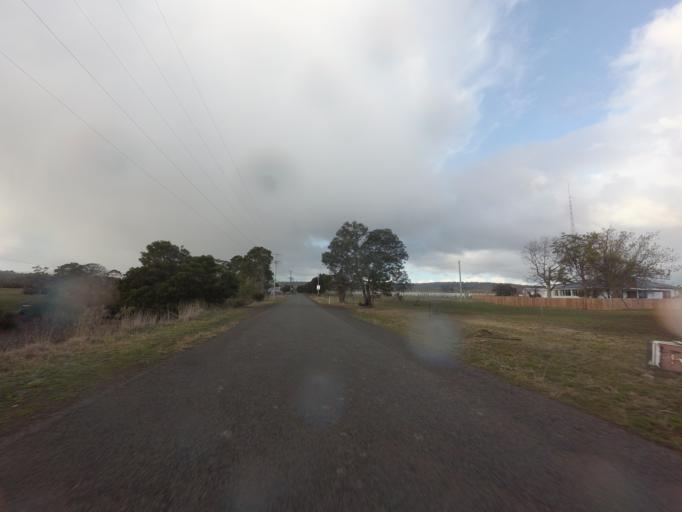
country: AU
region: Tasmania
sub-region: Break O'Day
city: St Helens
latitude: -42.0054
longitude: 148.0809
